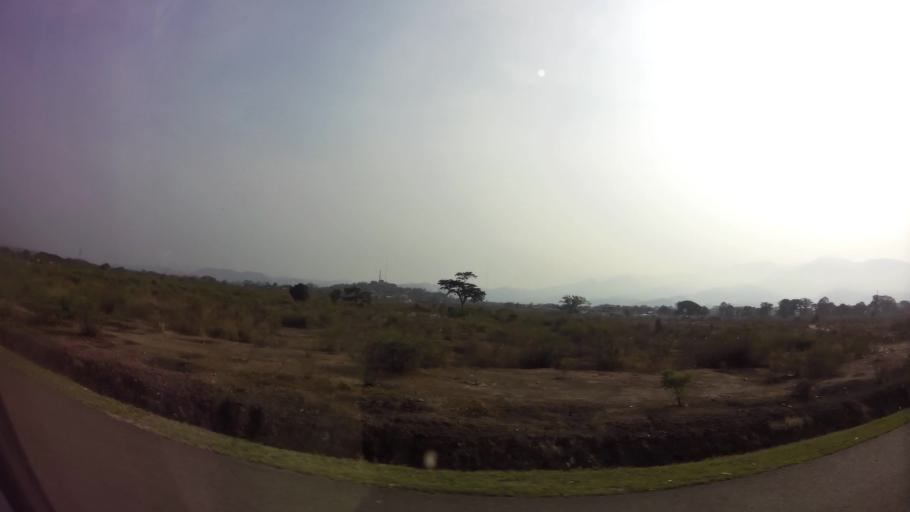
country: HN
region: Comayagua
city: Comayagua
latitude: 14.4313
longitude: -87.6458
